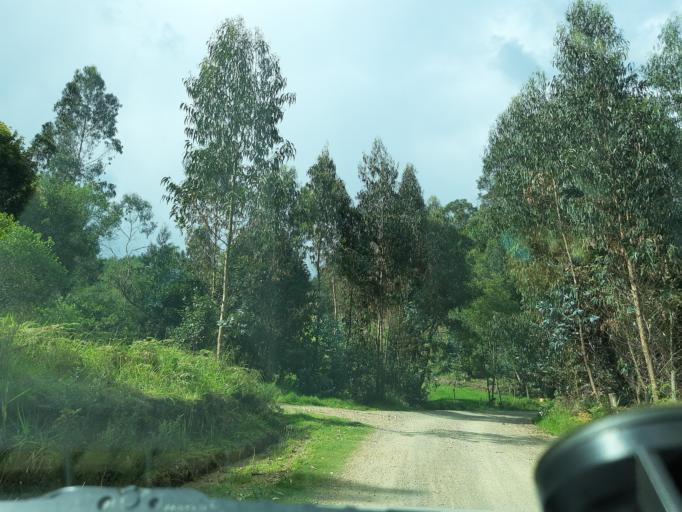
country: CO
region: Boyaca
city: Raquira
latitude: 5.5198
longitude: -73.6675
